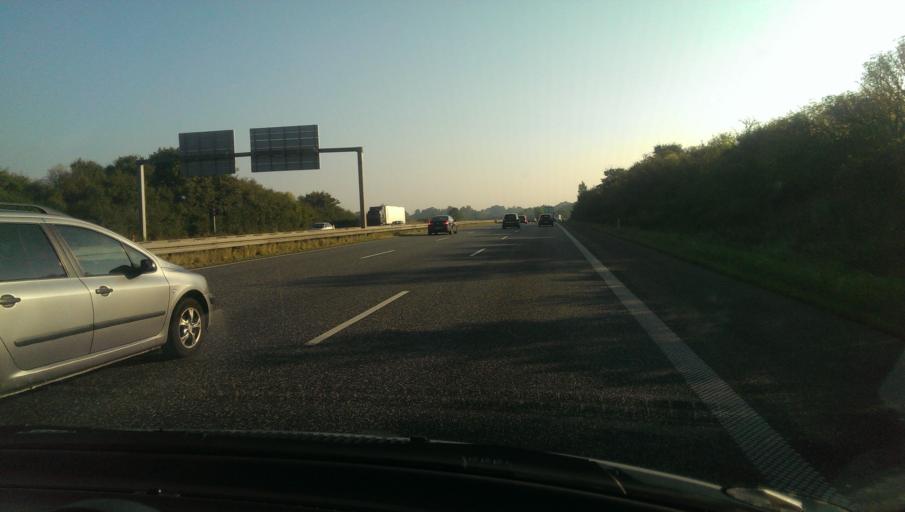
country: DK
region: South Denmark
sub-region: Kolding Kommune
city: Kolding
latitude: 55.5400
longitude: 9.5115
